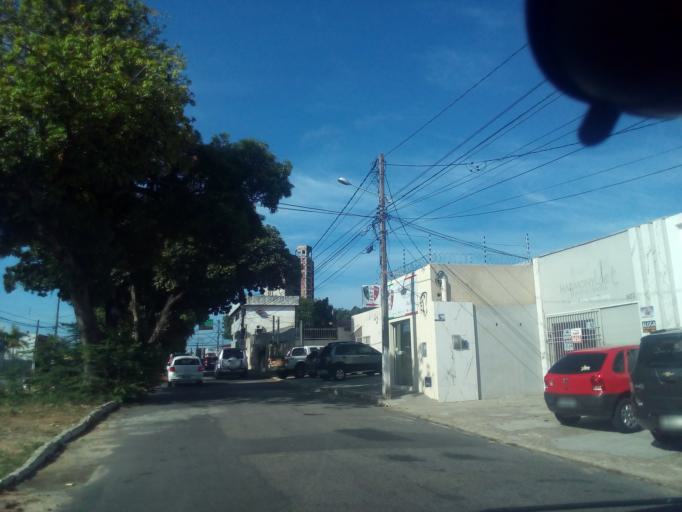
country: BR
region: Rio Grande do Norte
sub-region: Natal
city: Natal
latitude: -5.8167
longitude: -35.2141
